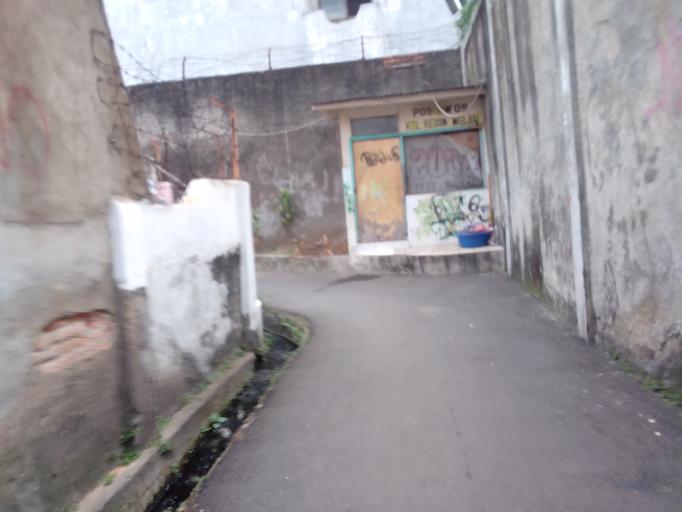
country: ID
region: Jakarta Raya
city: Jakarta
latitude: -6.1954
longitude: 106.8151
